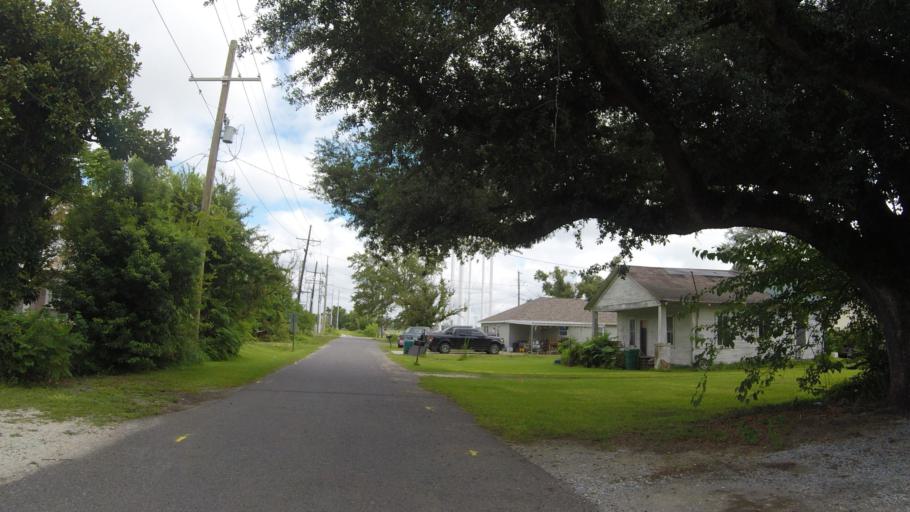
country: US
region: Louisiana
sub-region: Calcasieu Parish
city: Westlake
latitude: 30.2413
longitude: -93.2497
